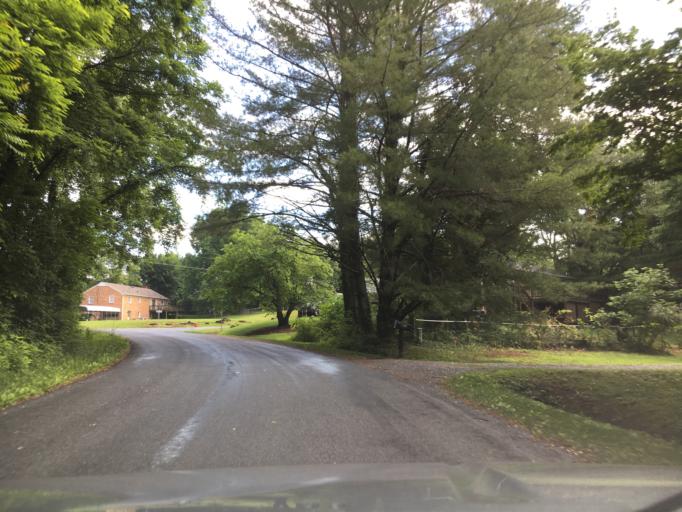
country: US
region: Virginia
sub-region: Bedford County
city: Forest
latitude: 37.3602
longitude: -79.2589
